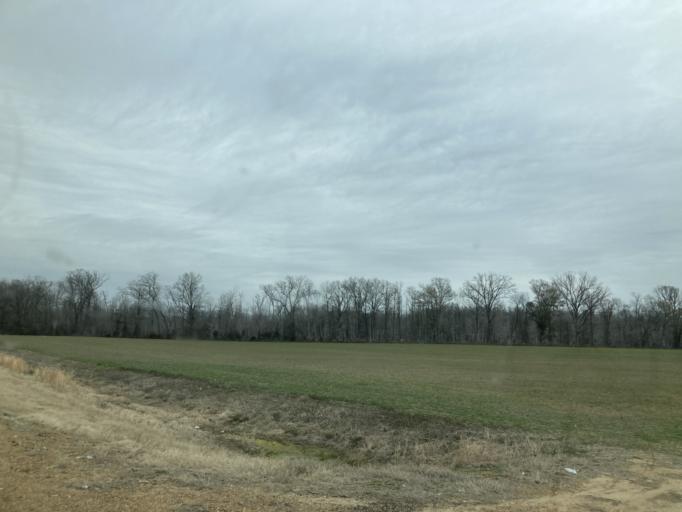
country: US
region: Mississippi
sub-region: Yazoo County
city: Yazoo City
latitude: 32.9860
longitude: -90.4648
